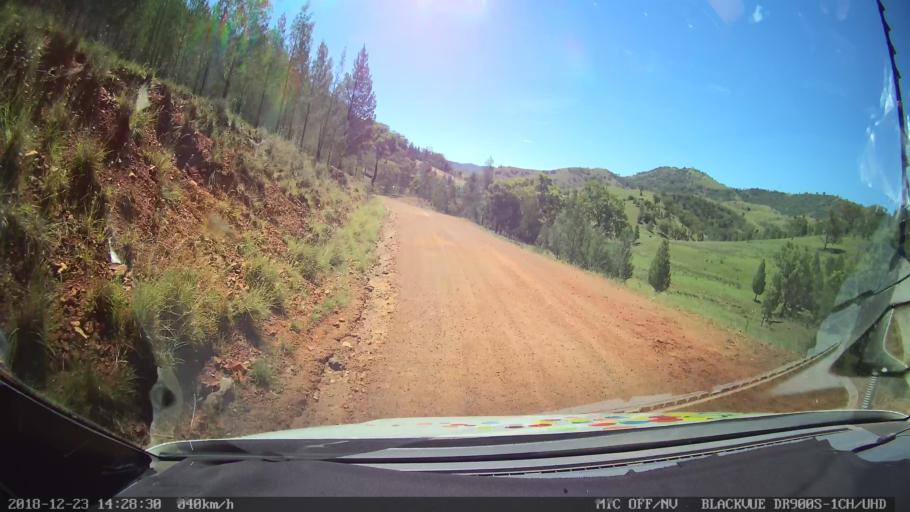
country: AU
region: New South Wales
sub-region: Tamworth Municipality
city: Manilla
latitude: -30.6139
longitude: 150.9415
